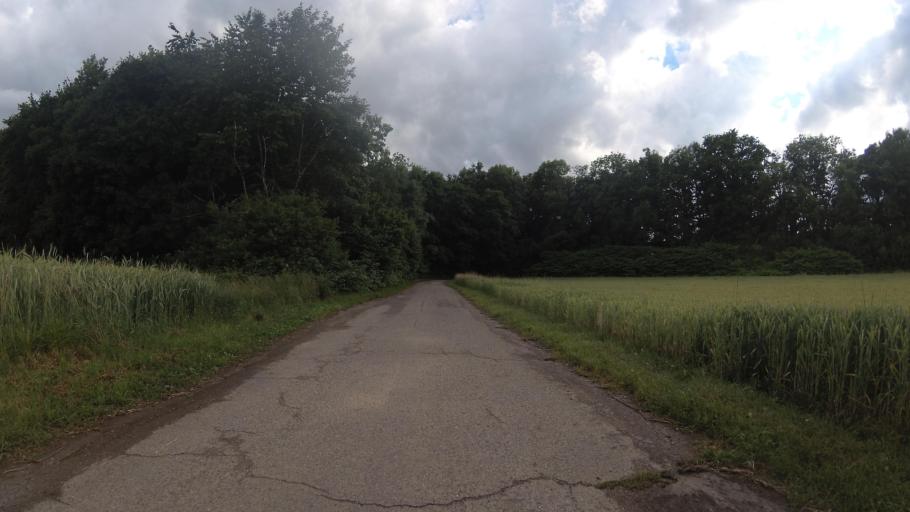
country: DE
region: Baden-Wuerttemberg
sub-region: Freiburg Region
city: Weil am Rhein
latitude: 47.5796
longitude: 7.6120
